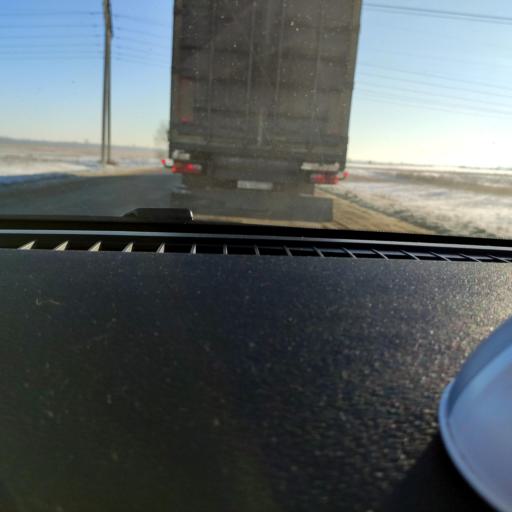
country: RU
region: Samara
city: Spiridonovka
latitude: 53.1422
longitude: 50.5951
